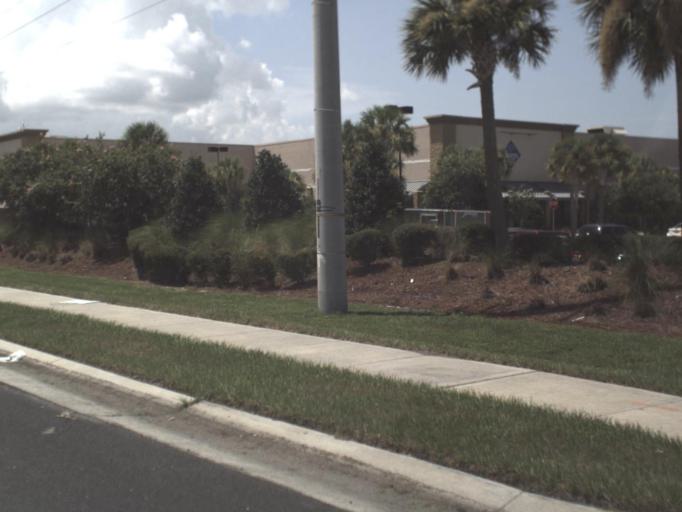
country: US
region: Florida
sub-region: Hillsborough County
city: Sun City Center
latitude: 27.7902
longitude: -82.3350
